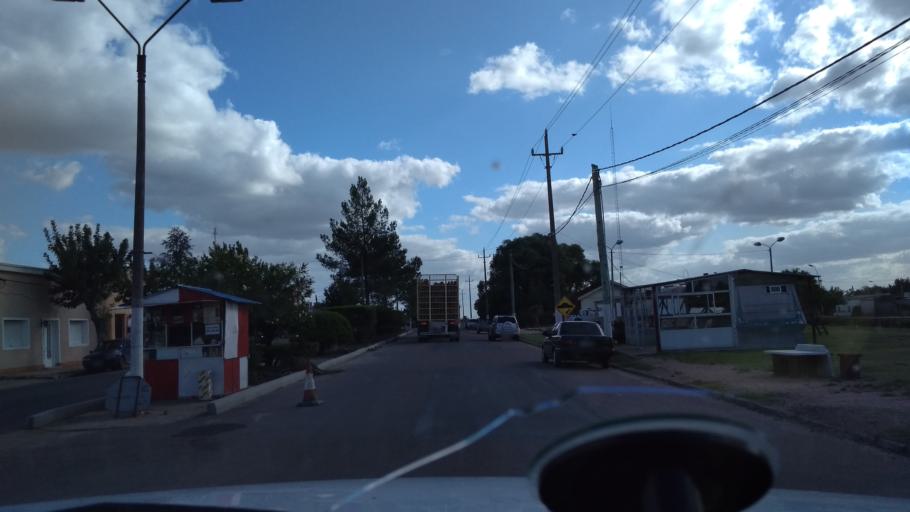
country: UY
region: Florida
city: Casupa
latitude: -34.1001
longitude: -55.6533
